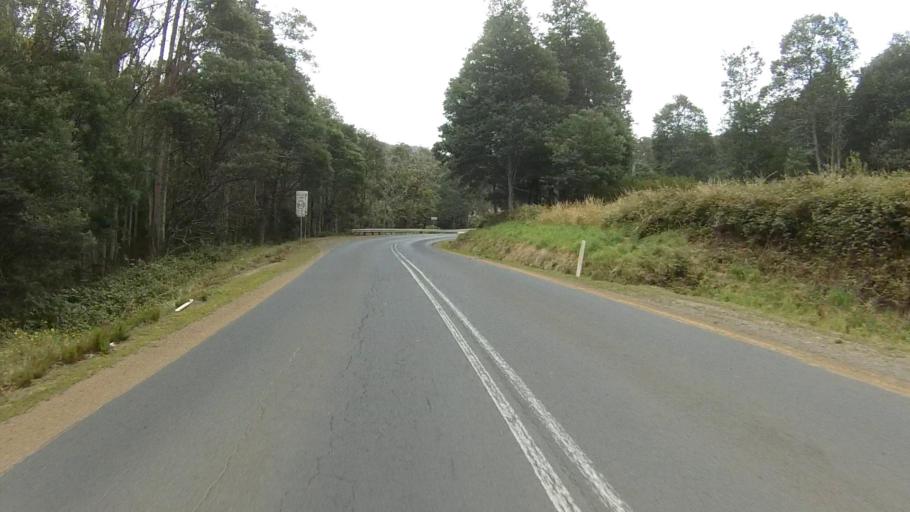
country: AU
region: Tasmania
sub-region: Huon Valley
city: Cygnet
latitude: -43.1440
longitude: 147.1535
